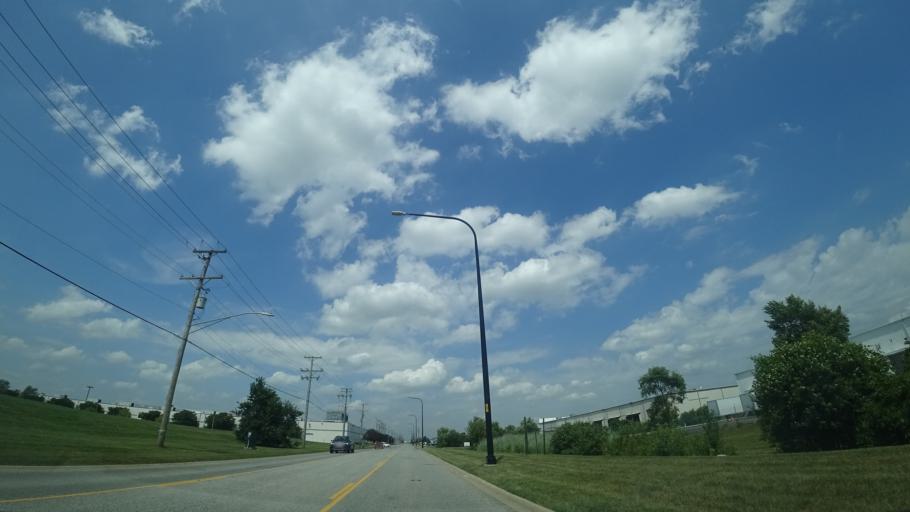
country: US
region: Illinois
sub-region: Cook County
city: Crestwood
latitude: 41.6765
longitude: -87.7587
